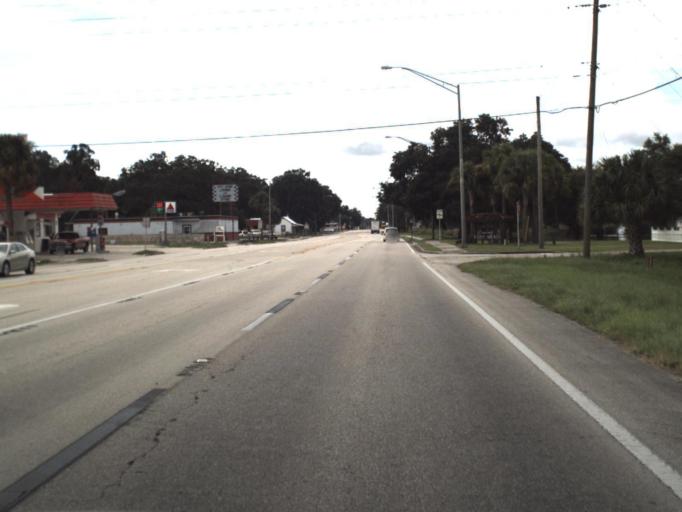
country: US
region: Florida
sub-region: Polk County
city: Fort Meade
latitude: 27.7630
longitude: -81.8016
